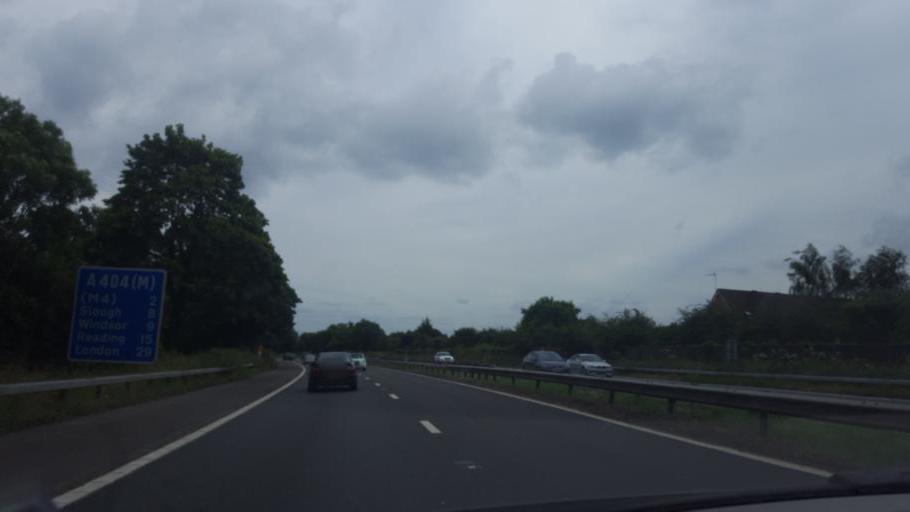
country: GB
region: England
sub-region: Royal Borough of Windsor and Maidenhead
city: White Waltham
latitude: 51.5151
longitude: -0.7613
